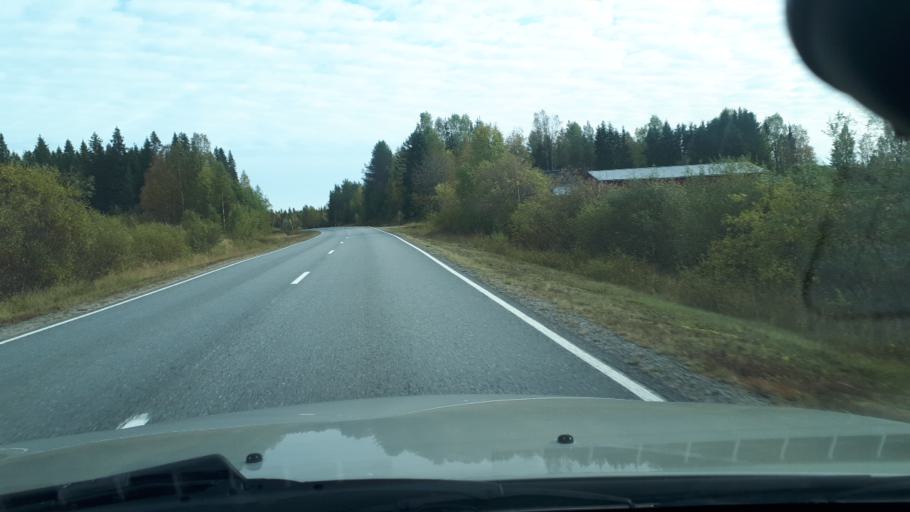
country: FI
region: Lapland
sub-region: Rovaniemi
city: Rovaniemi
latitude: 65.9542
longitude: 25.9269
